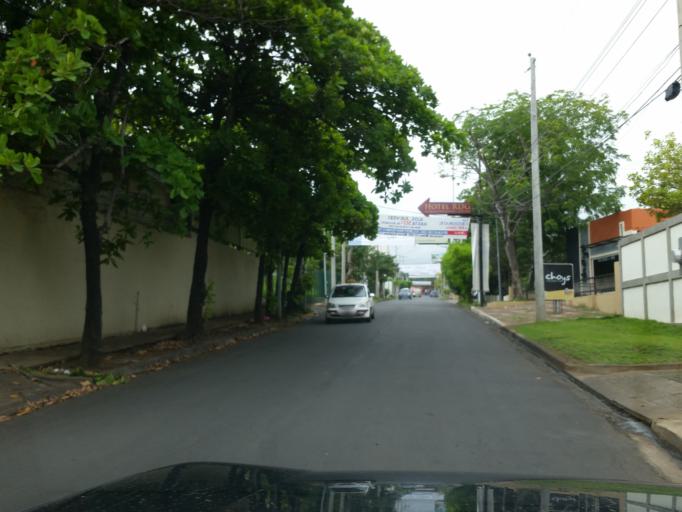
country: NI
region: Managua
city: Managua
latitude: 12.1152
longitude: -86.2634
